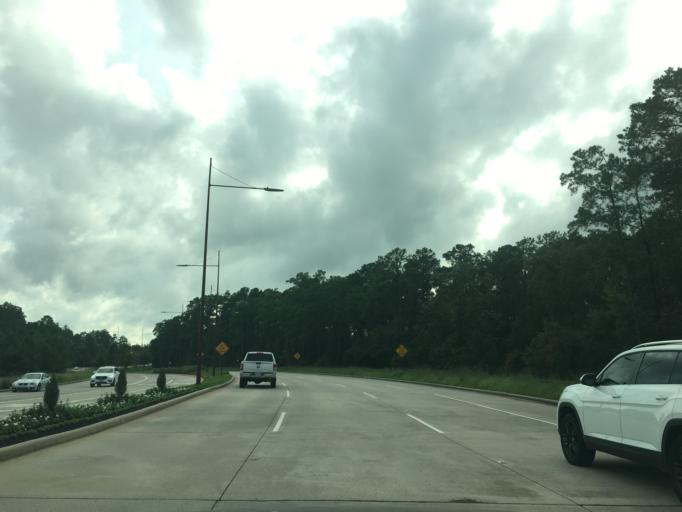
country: US
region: Texas
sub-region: Harris County
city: Spring
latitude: 30.1049
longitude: -95.4396
